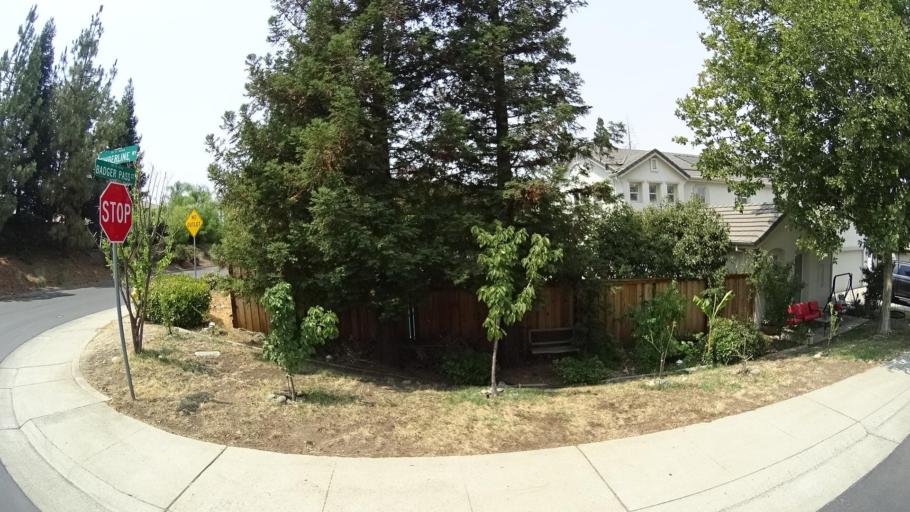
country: US
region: California
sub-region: Placer County
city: Rocklin
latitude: 38.7959
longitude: -121.2789
